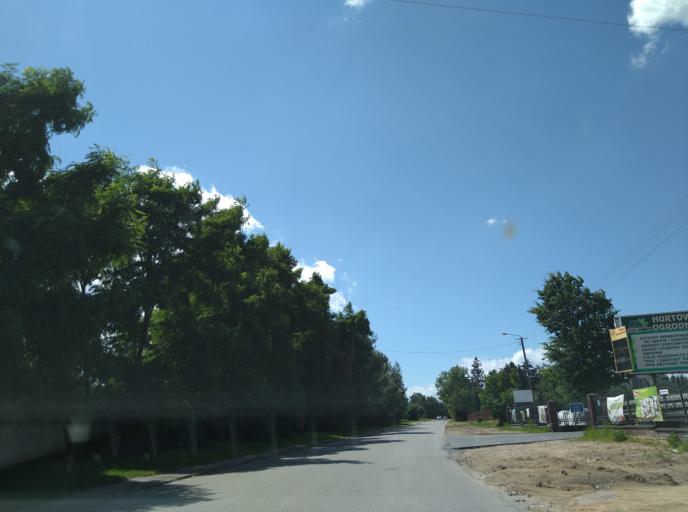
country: PL
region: Masovian Voivodeship
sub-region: Powiat bialobrzeski
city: Promna
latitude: 51.6722
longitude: 20.9350
